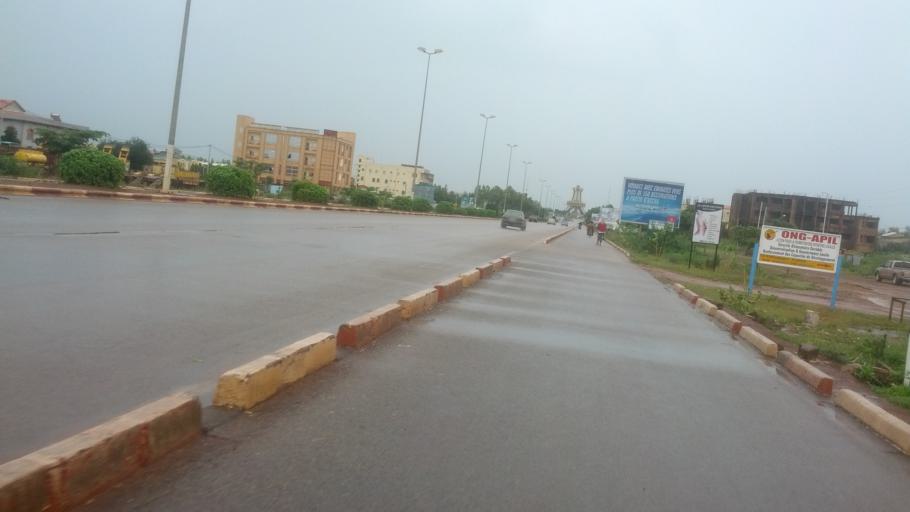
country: BF
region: Centre
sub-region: Kadiogo Province
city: Ouagadougou
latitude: 12.3246
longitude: -1.5027
